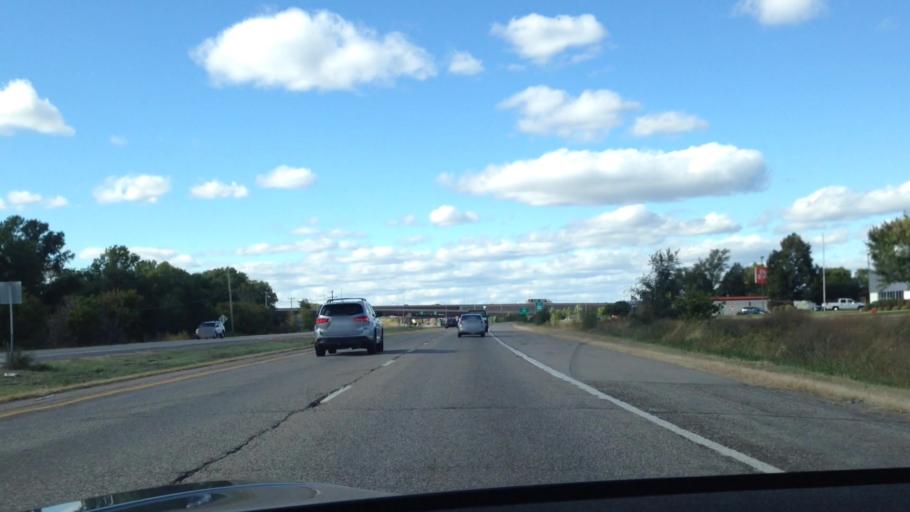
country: US
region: Minnesota
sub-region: Hennepin County
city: Osseo
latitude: 45.1012
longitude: -93.3892
